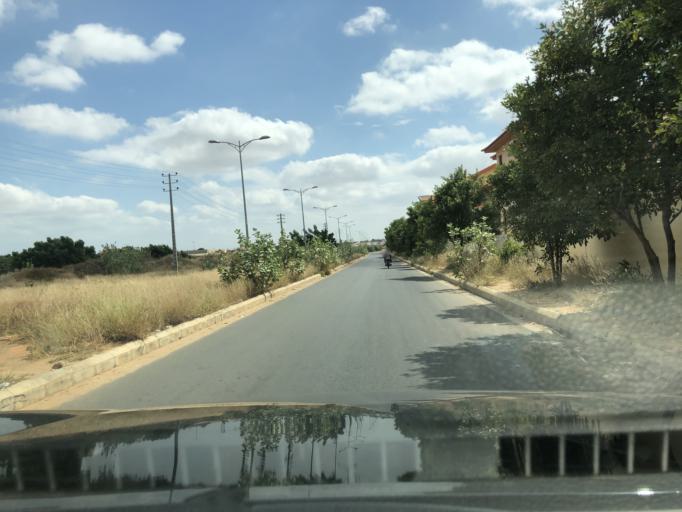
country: AO
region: Luanda
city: Luanda
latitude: -8.9477
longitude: 13.2426
